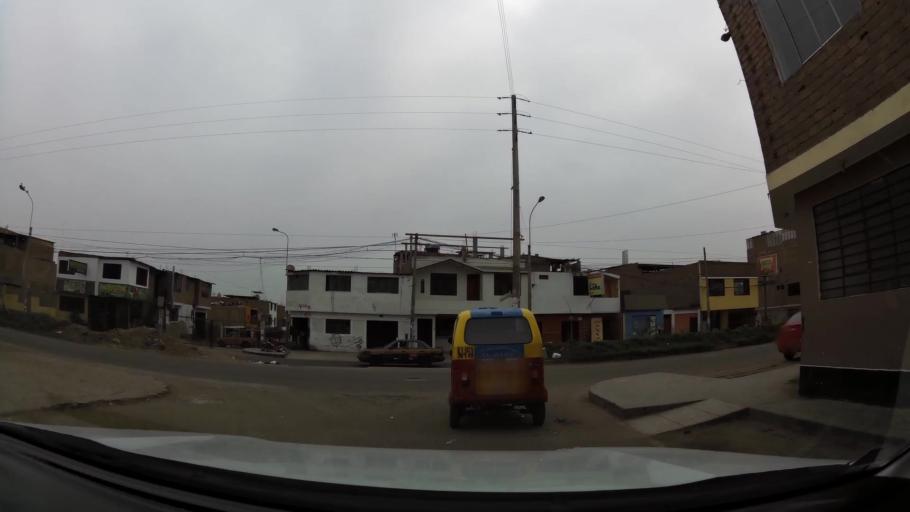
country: PE
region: Lima
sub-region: Lima
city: Surco
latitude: -12.1759
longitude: -76.9666
